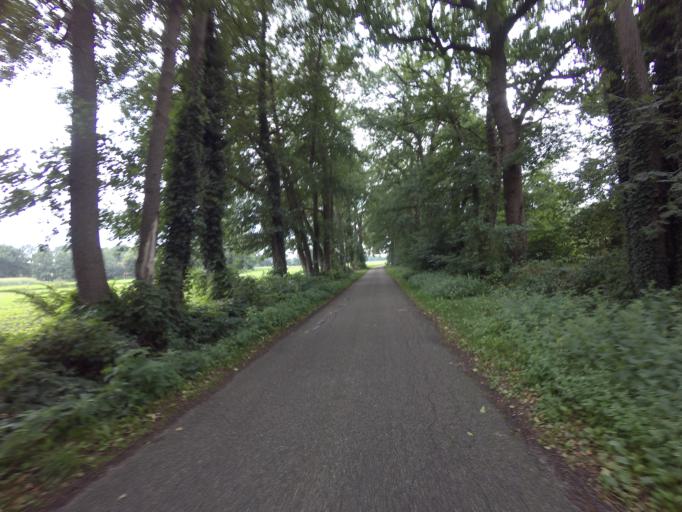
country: DE
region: Lower Saxony
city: Lage
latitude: 52.4621
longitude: 6.9167
